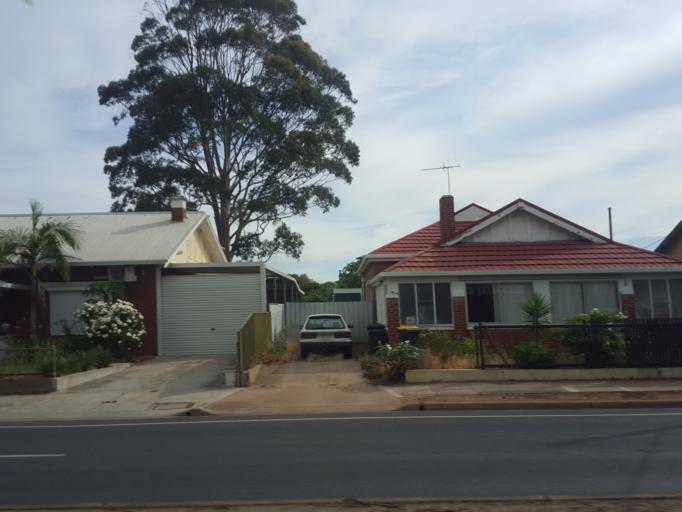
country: AU
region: South Australia
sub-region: Charles Sturt
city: Woodville
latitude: -34.8824
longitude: 138.5603
